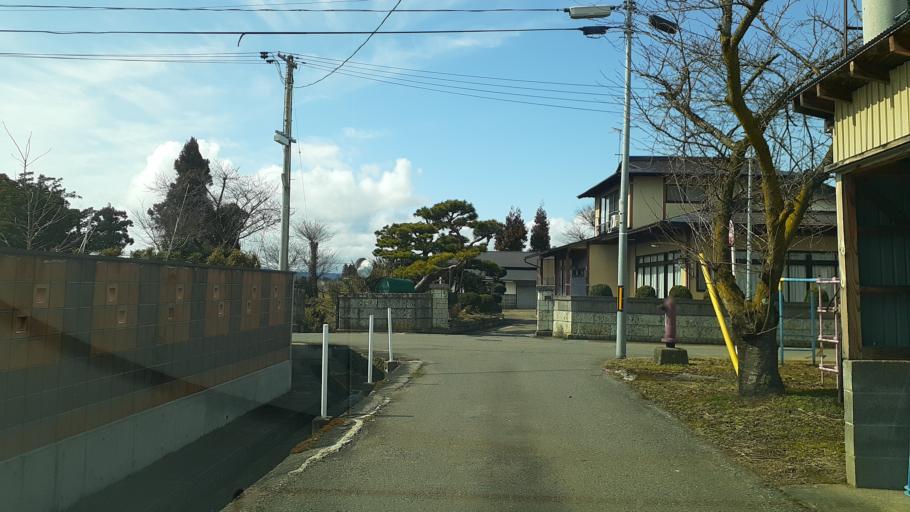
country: JP
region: Fukushima
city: Kitakata
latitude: 37.5625
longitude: 139.8906
